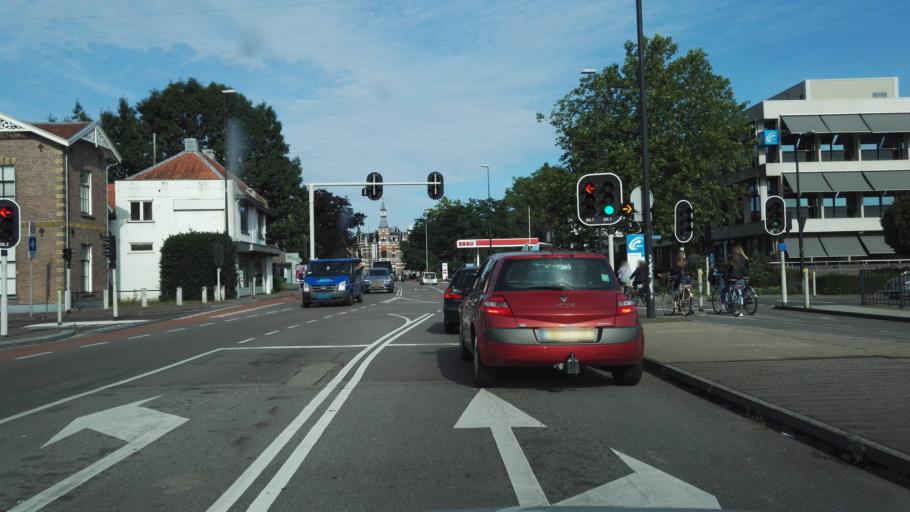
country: NL
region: Gelderland
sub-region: Gemeente Apeldoorn
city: Apeldoorn
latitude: 52.2168
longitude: 5.9703
